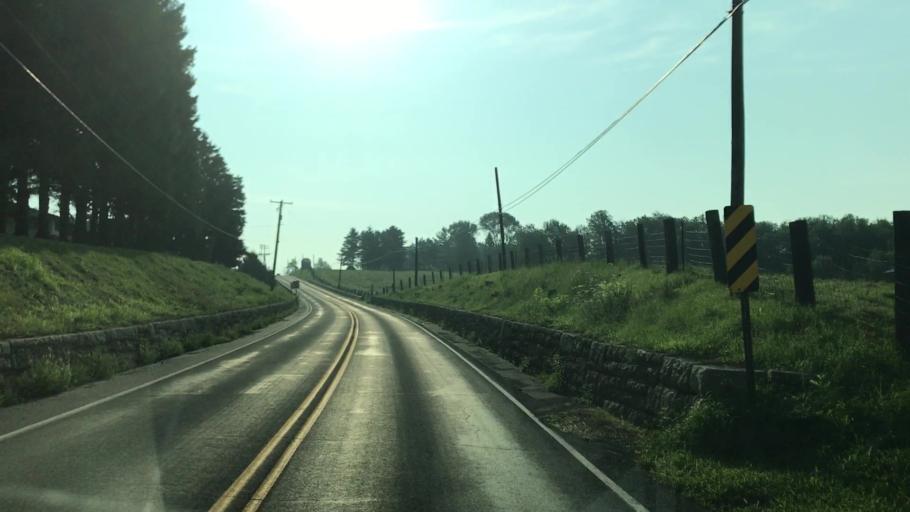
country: US
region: Pennsylvania
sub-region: Lackawanna County
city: Dalton
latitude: 41.5979
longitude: -75.7124
